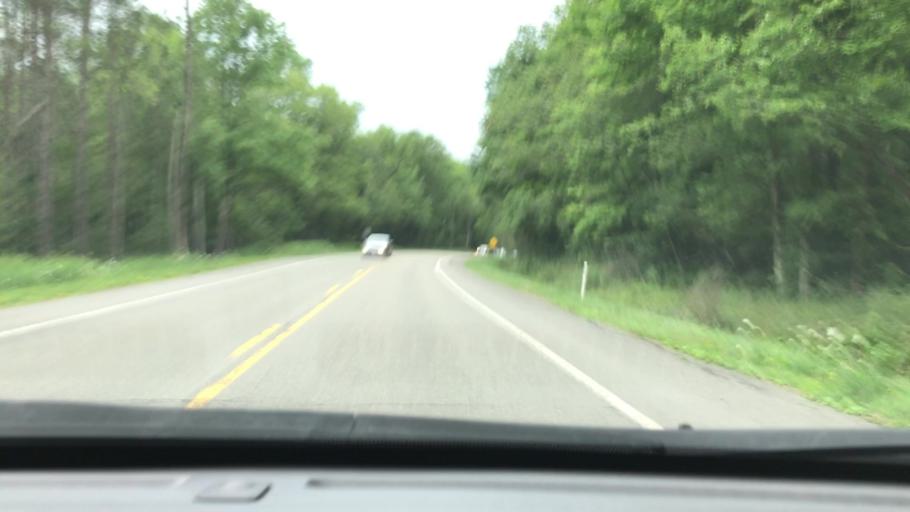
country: US
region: Pennsylvania
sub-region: McKean County
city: Bradford
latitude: 41.8413
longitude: -78.6925
